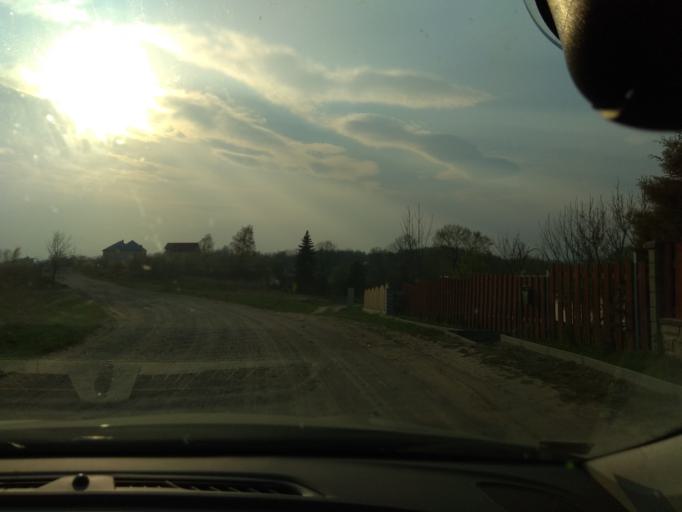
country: LT
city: Baltoji Voke
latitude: 54.5951
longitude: 25.1646
